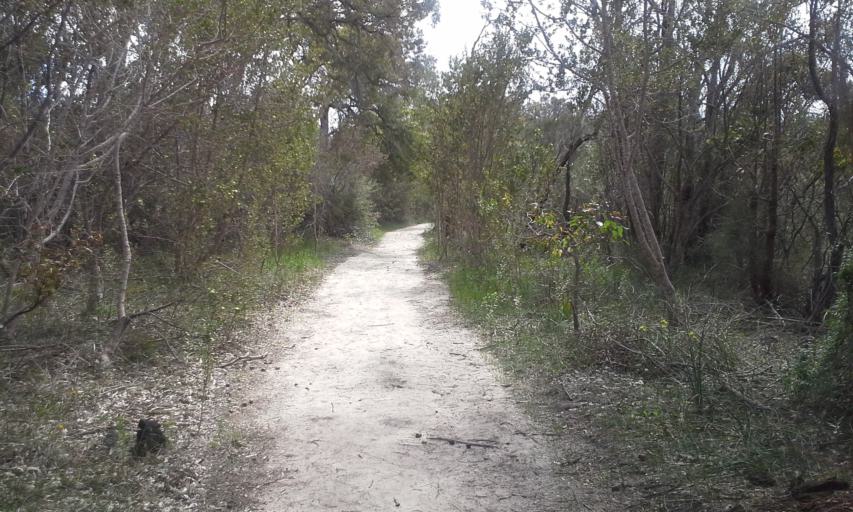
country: AU
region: Western Australia
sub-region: City of Perth
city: West Perth
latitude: -31.9606
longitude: 115.8358
